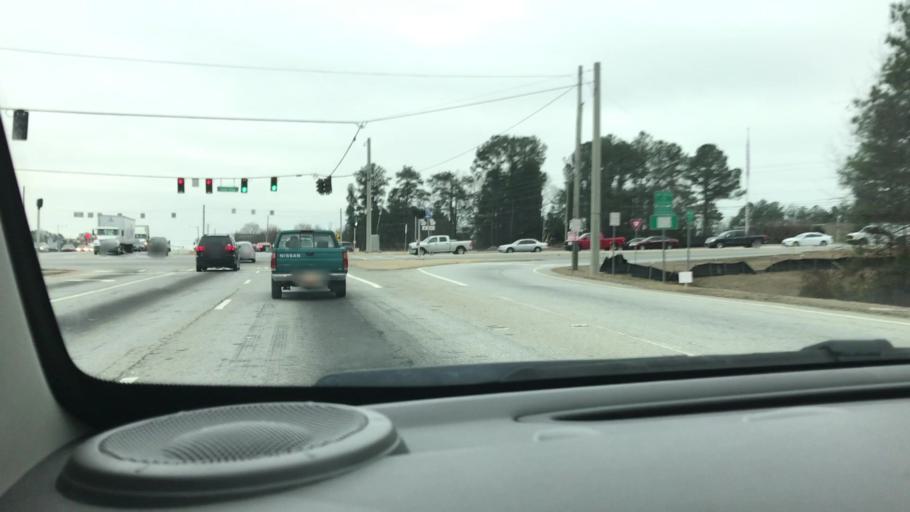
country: US
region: Georgia
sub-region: Clayton County
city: Forest Park
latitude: 33.6159
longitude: -84.4028
